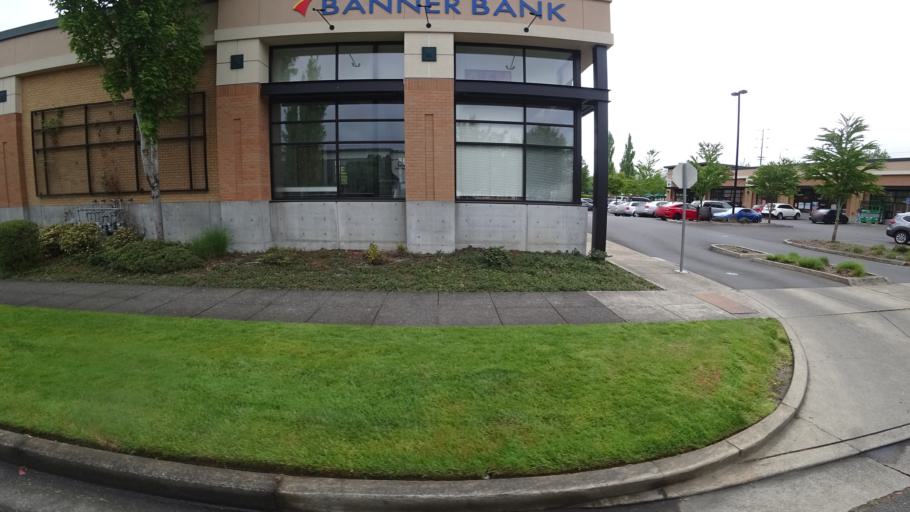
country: US
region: Oregon
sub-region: Washington County
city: Rockcreek
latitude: 45.5351
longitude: -122.8772
